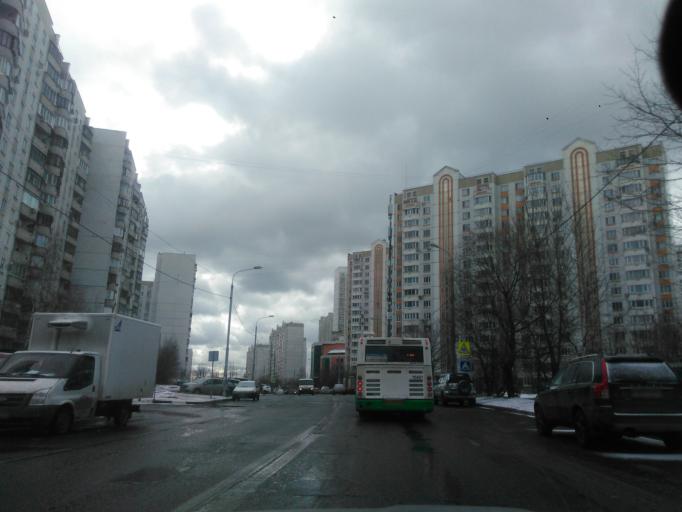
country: RU
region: Moskovskaya
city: Krasnogorsk
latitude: 55.8478
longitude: 37.3443
